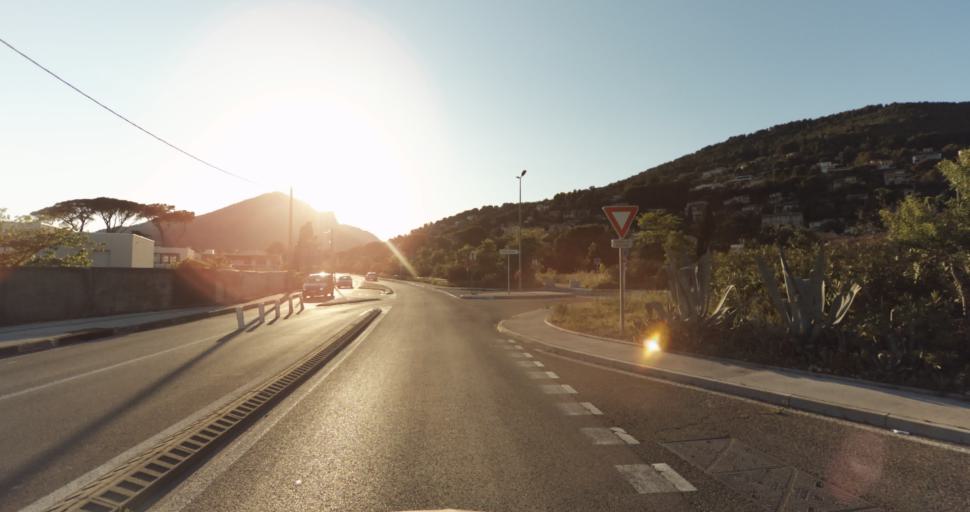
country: FR
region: Provence-Alpes-Cote d'Azur
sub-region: Departement du Var
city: La Valette-du-Var
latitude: 43.1420
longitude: 6.0001
